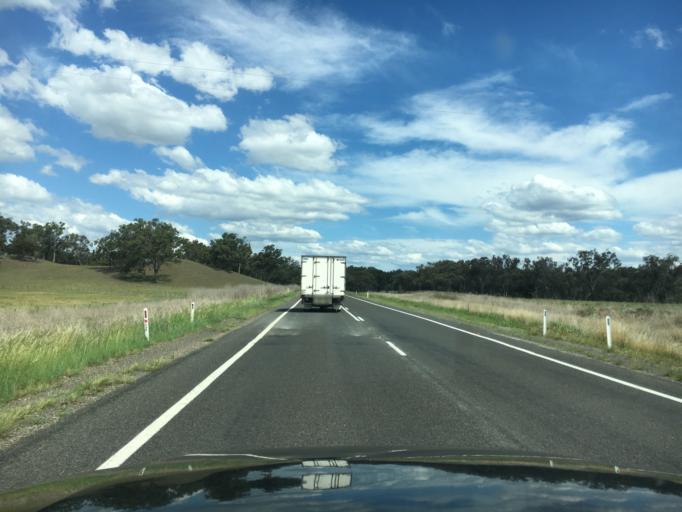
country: AU
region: New South Wales
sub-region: Liverpool Plains
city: Quirindi
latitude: -31.4809
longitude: 150.8625
